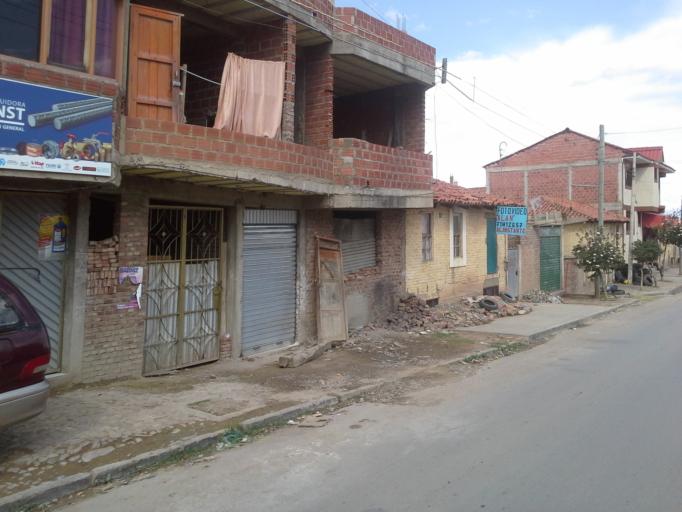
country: BO
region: Cochabamba
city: Tarata
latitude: -17.6103
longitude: -66.0223
